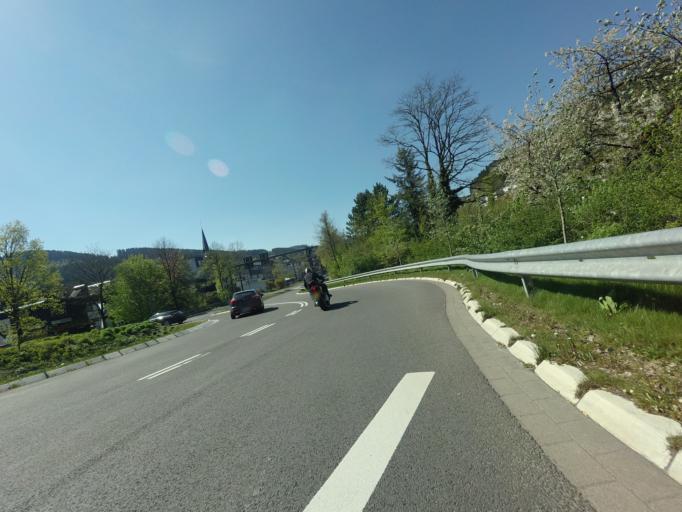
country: DE
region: North Rhine-Westphalia
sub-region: Regierungsbezirk Arnsberg
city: Lennestadt
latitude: 51.1068
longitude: 8.0736
